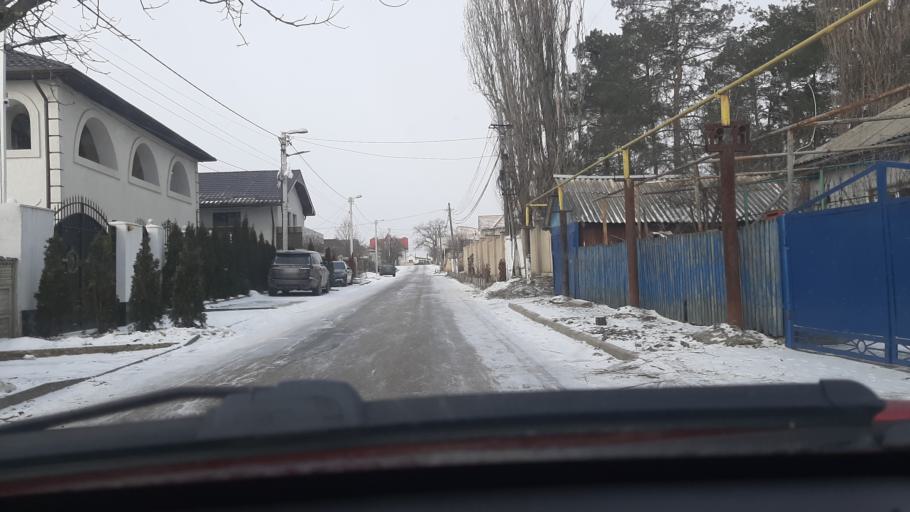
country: MD
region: Laloveni
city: Ialoveni
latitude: 46.9926
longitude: 28.7809
